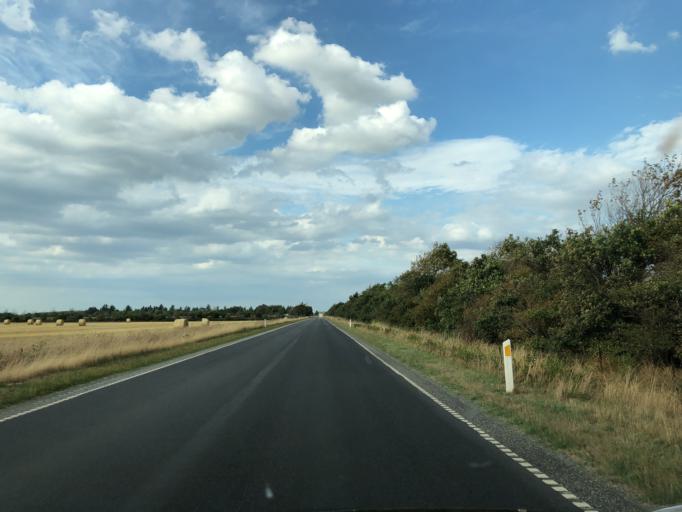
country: DK
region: Central Jutland
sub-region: Holstebro Kommune
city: Holstebro
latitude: 56.3791
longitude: 8.4483
